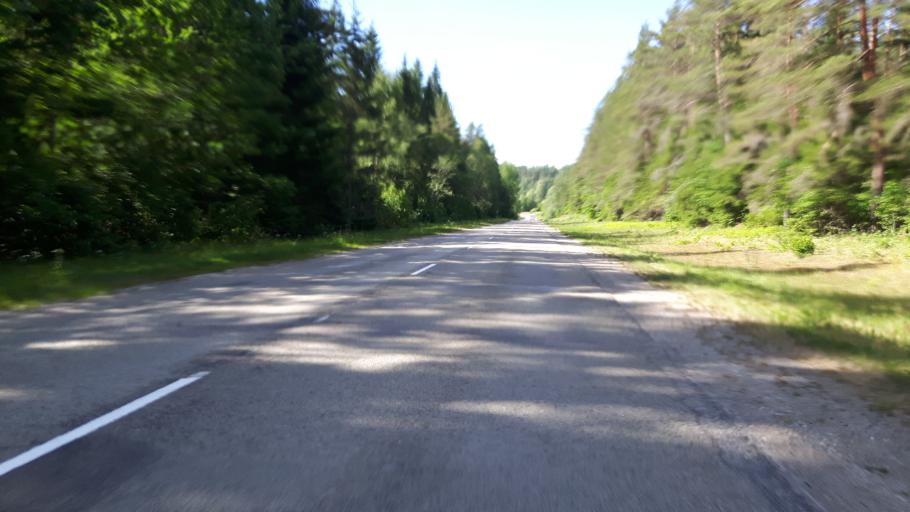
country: LV
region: Talsu Rajons
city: Sabile
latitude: 57.0804
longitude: 22.5282
